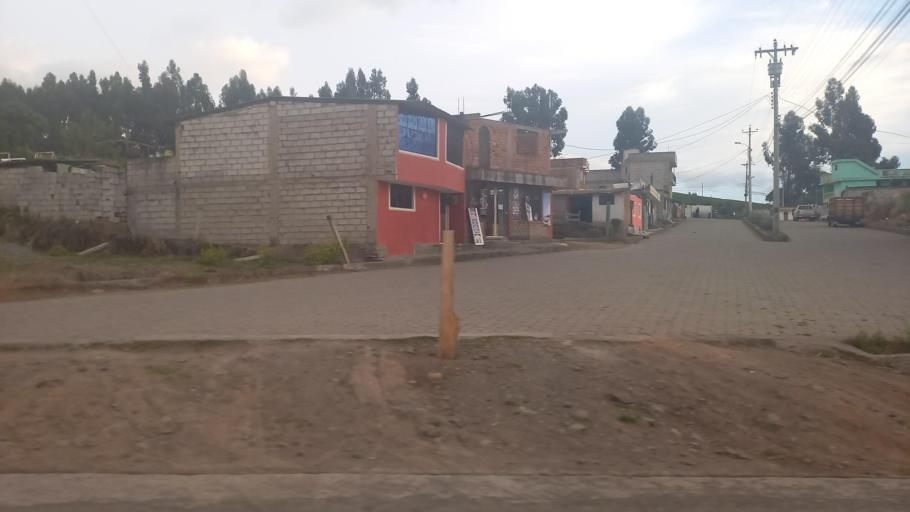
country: EC
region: Pichincha
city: Cayambe
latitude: 0.0913
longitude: -78.0992
